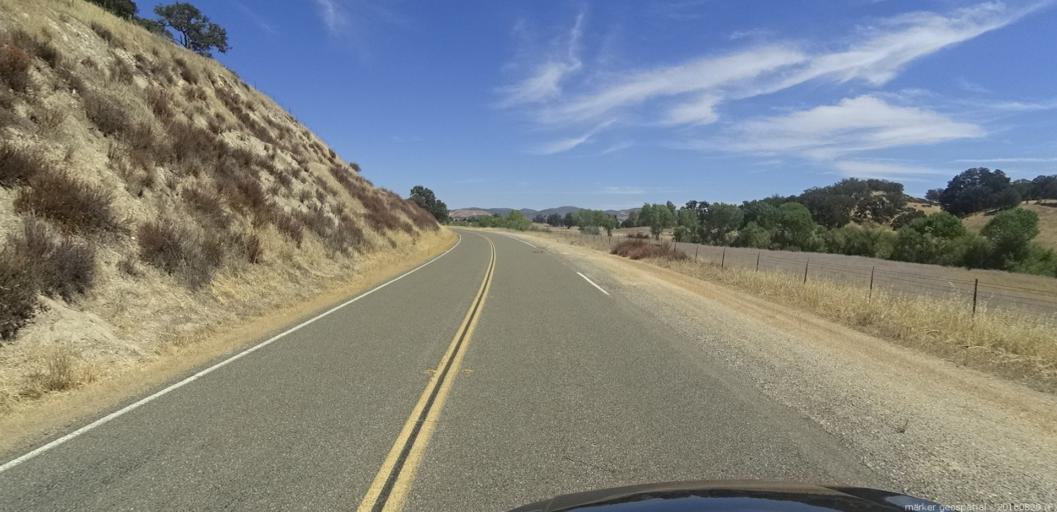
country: US
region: California
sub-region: San Luis Obispo County
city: Lake Nacimiento
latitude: 35.9153
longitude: -121.0846
